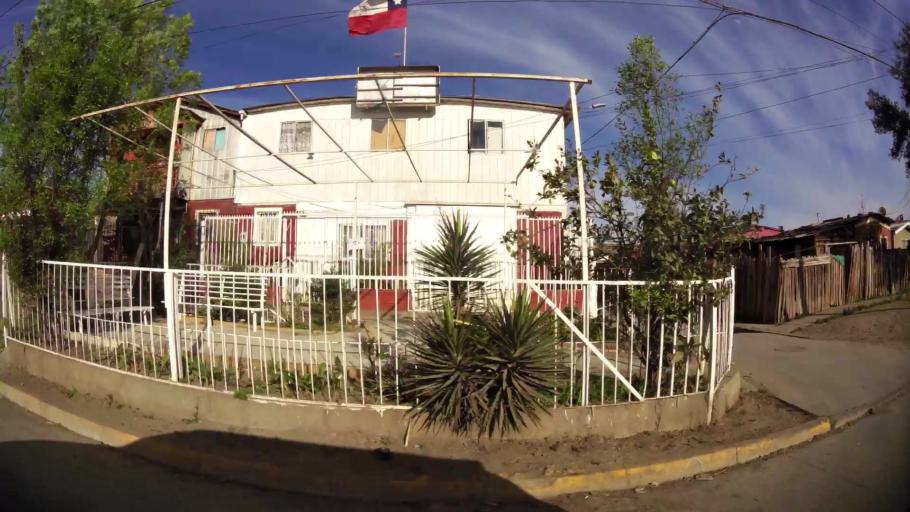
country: CL
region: Santiago Metropolitan
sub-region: Provincia de Santiago
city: Lo Prado
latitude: -33.4747
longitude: -70.6982
